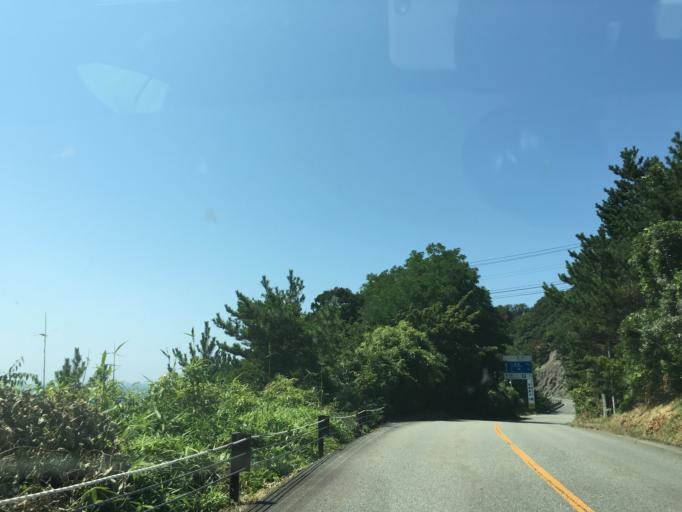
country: JP
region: Akita
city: Tenno
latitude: 39.9121
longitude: 139.7281
